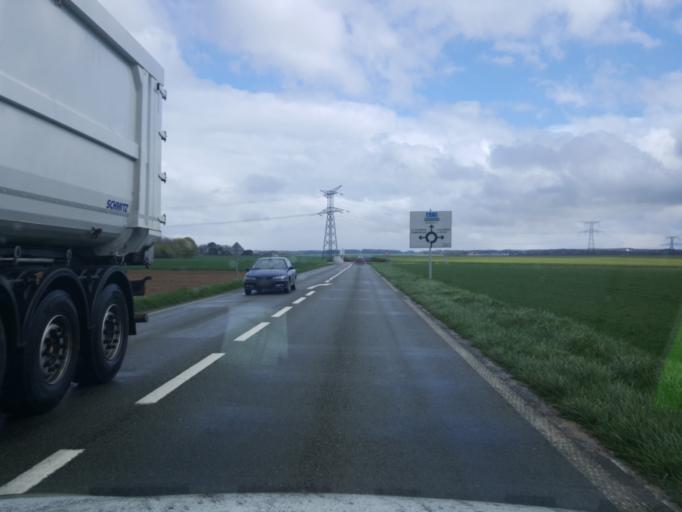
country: FR
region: Picardie
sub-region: Departement de l'Oise
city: Chaumont-en-Vexin
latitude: 49.3154
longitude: 1.8839
